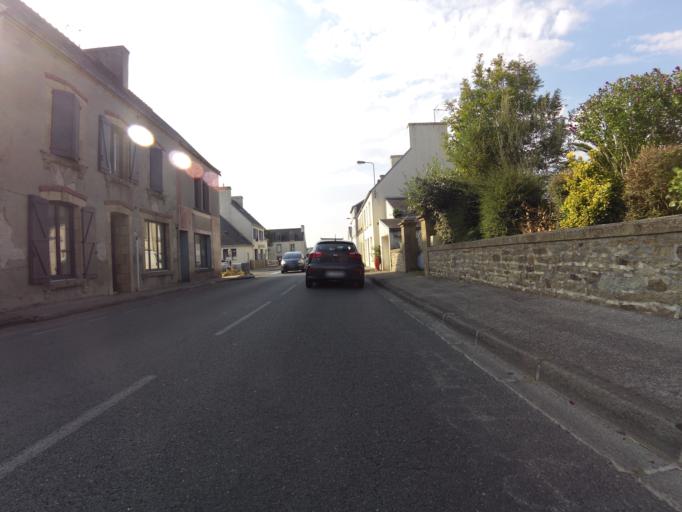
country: FR
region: Brittany
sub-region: Departement du Finistere
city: Pouldreuzic
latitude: 47.9567
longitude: -4.3619
